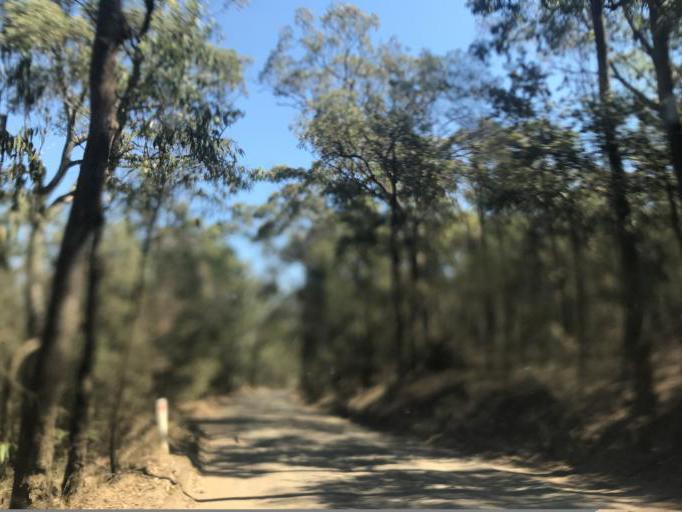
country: AU
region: New South Wales
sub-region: Hawkesbury
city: Pitt Town
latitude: -33.4627
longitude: 150.8371
